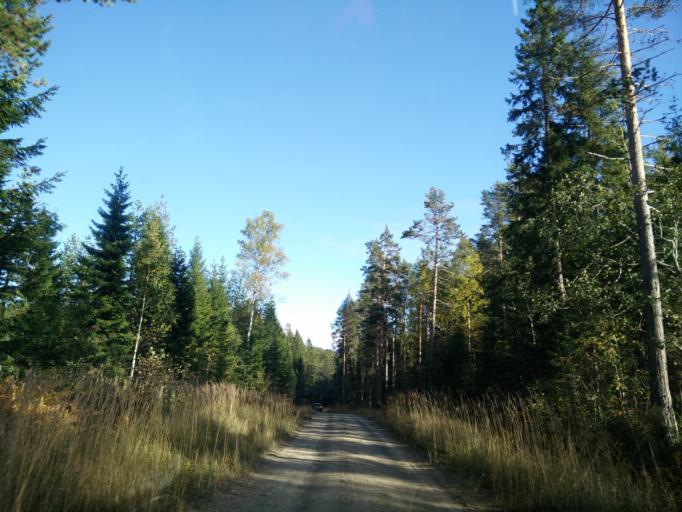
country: SE
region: Vaesternorrland
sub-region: Sundsvalls Kommun
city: Matfors
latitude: 62.3360
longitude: 16.8843
